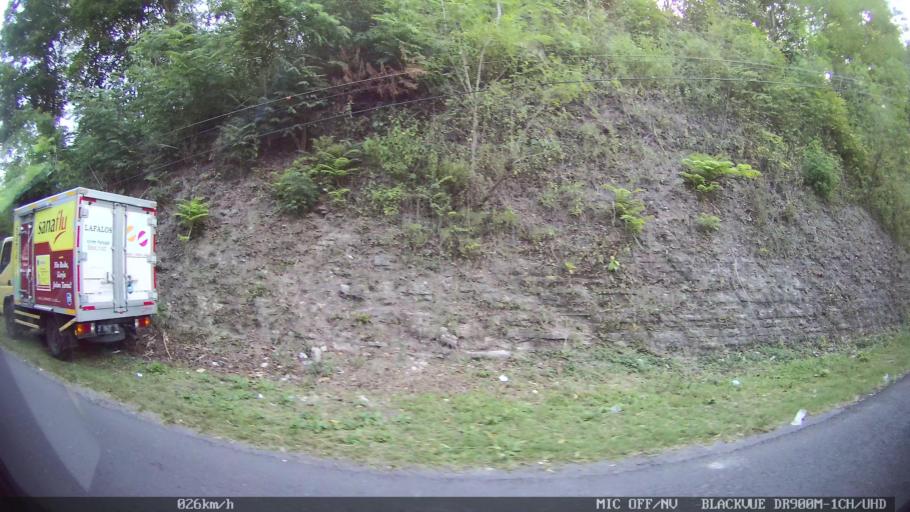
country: ID
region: Daerah Istimewa Yogyakarta
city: Bantul
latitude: -7.8757
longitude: 110.3151
